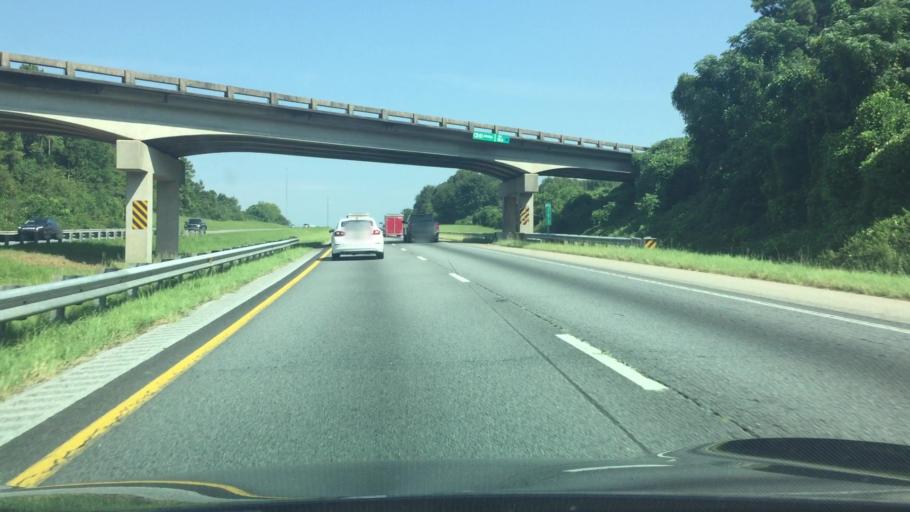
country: US
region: Alabama
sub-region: Autauga County
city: Pine Level
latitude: 32.6124
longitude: -86.4808
